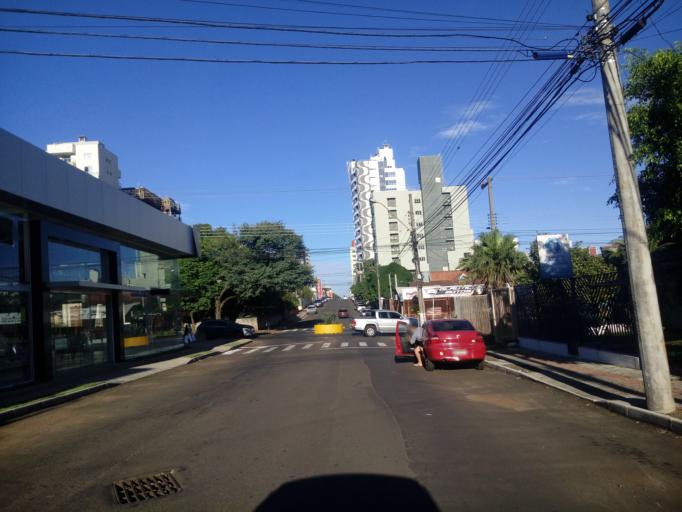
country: BR
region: Santa Catarina
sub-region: Chapeco
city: Chapeco
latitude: -27.0933
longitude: -52.6134
